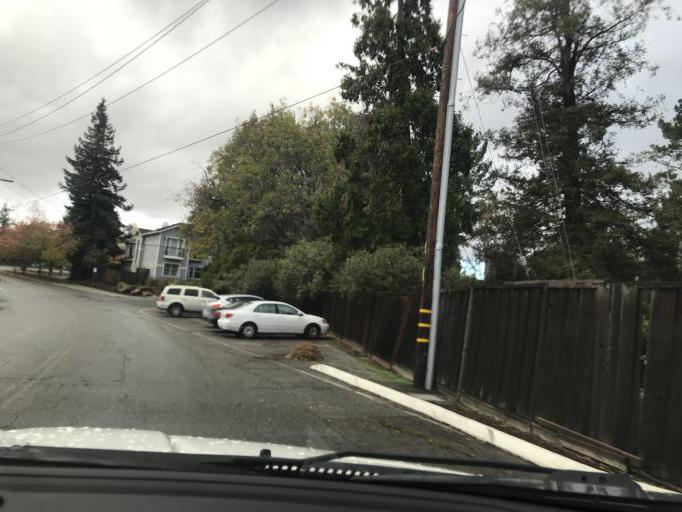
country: US
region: California
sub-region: Santa Clara County
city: Buena Vista
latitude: 37.2949
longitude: -121.9086
